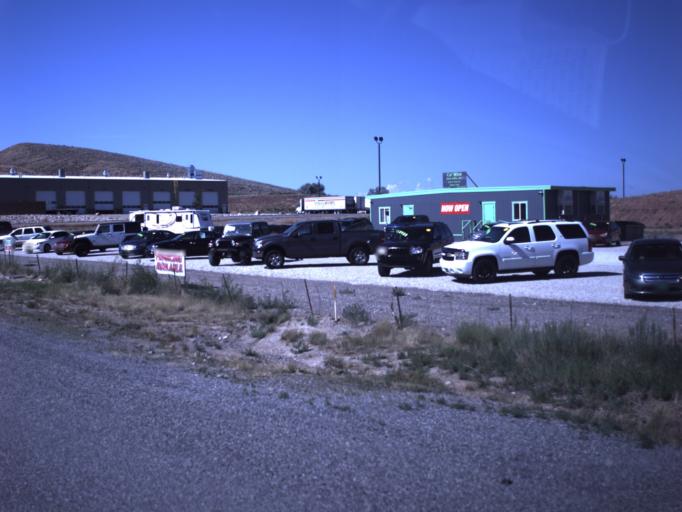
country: US
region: Utah
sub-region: Sevier County
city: Salina
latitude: 38.9416
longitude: -111.8546
